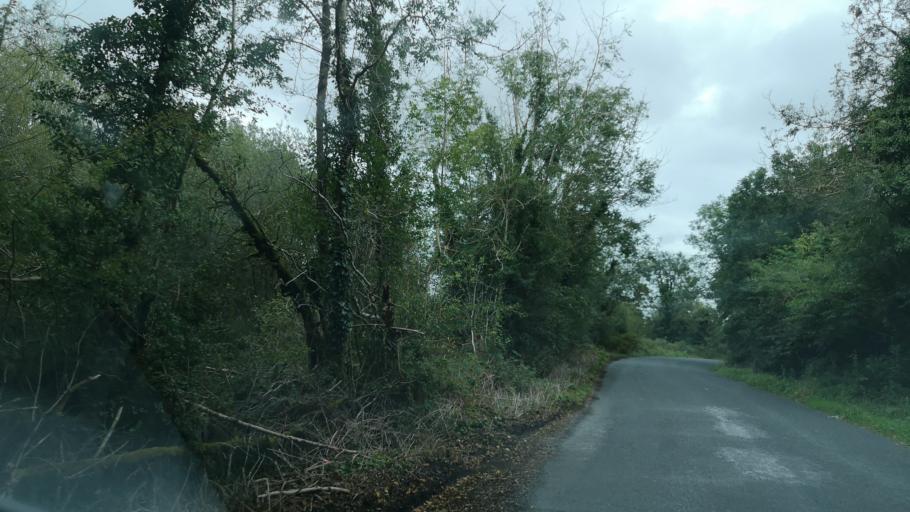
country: IE
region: Connaught
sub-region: County Galway
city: Loughrea
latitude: 53.2885
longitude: -8.5908
